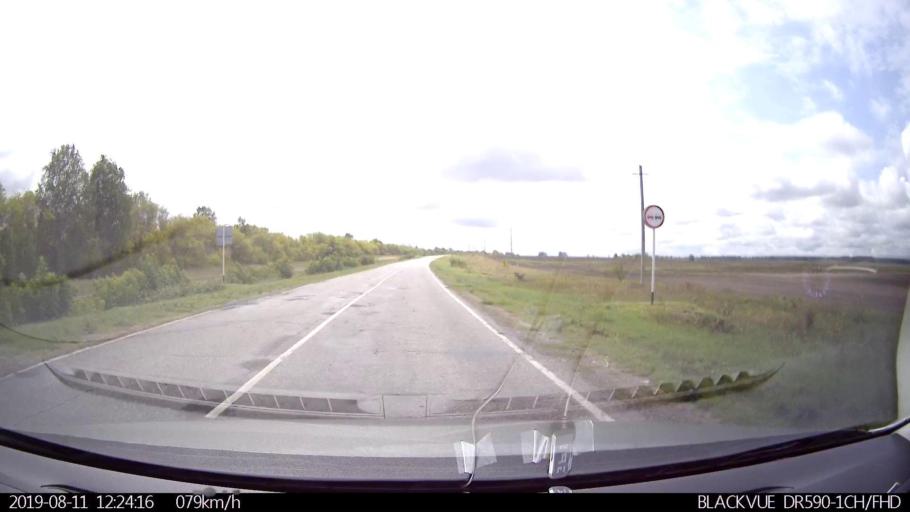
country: RU
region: Ulyanovsk
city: Ignatovka
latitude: 53.8852
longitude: 47.9495
